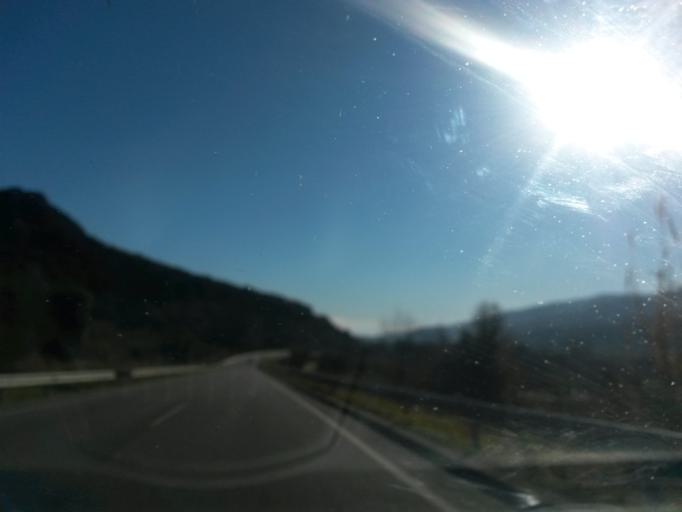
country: ES
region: Catalonia
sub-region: Provincia de Girona
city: les Planes d'Hostoles
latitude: 42.0670
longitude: 2.5276
